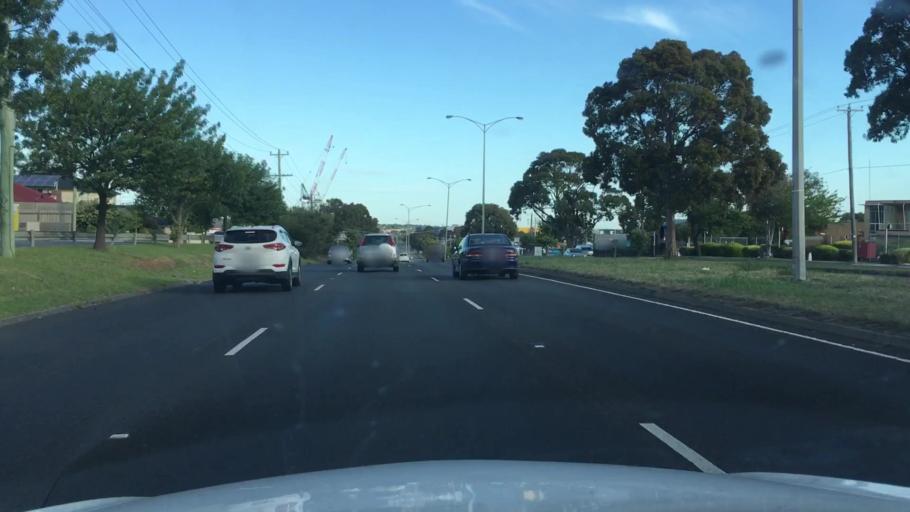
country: AU
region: Victoria
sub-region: Monash
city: Clayton
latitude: -37.9180
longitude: 145.1330
